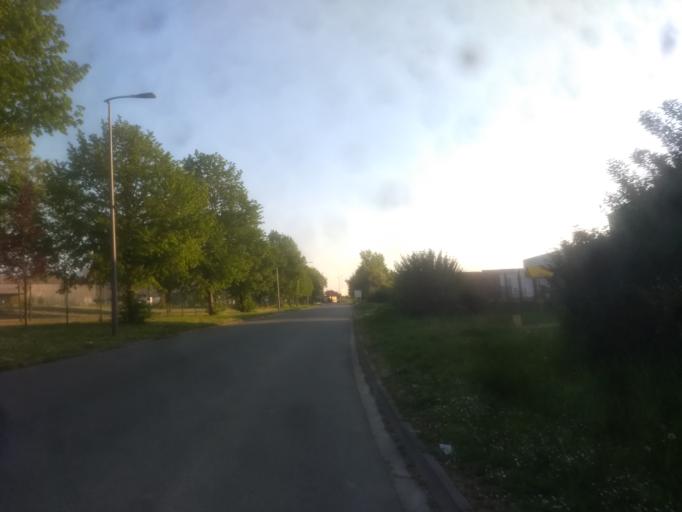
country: FR
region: Nord-Pas-de-Calais
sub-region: Departement du Pas-de-Calais
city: Saint-Laurent-Blangy
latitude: 50.2888
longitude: 2.8142
